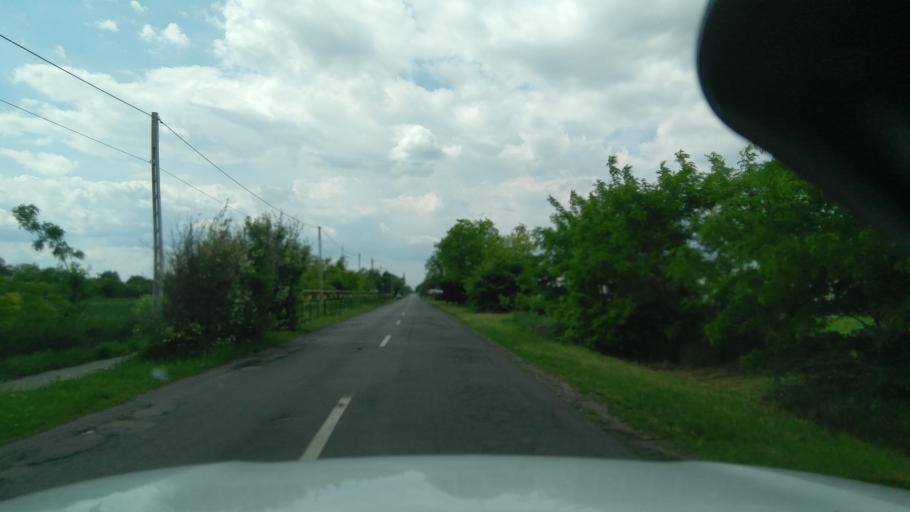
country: HU
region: Bekes
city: Magyarbanhegyes
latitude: 46.4489
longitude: 20.9772
